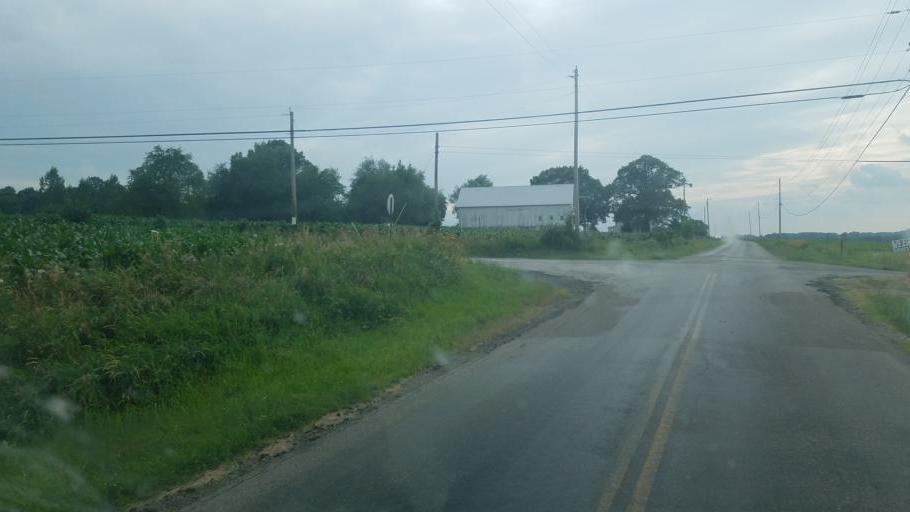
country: US
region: Ohio
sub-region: Wayne County
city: Dalton
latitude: 40.8241
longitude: -81.6763
